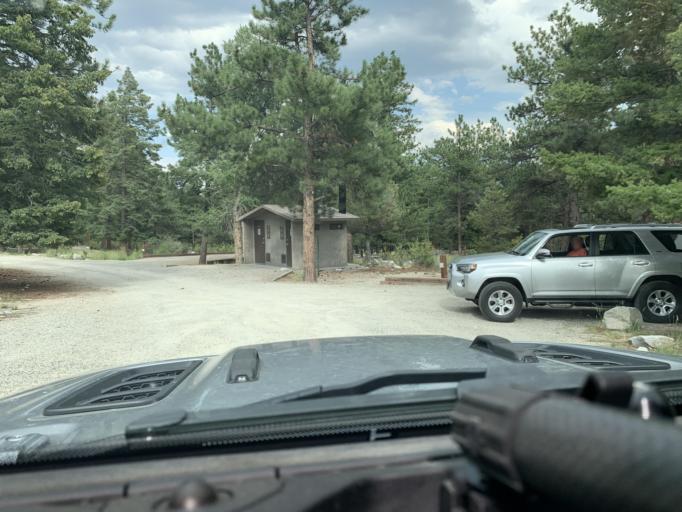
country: US
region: Colorado
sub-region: Chaffee County
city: Buena Vista
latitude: 38.7136
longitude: -106.2232
